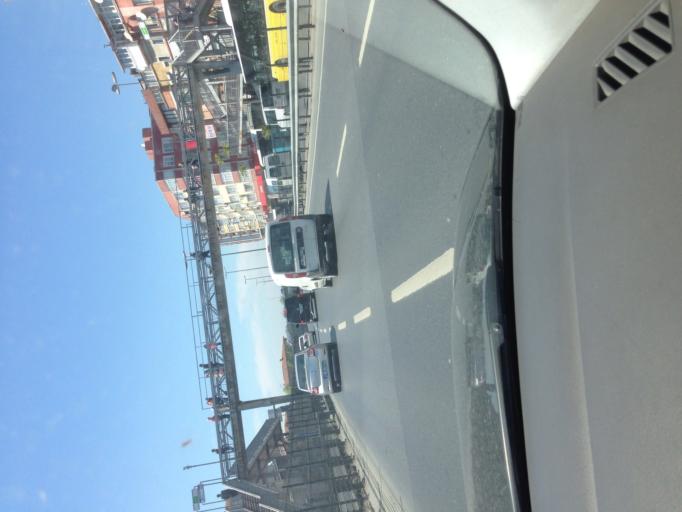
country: TR
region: Istanbul
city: Bahcelievler
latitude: 40.9856
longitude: 28.7830
